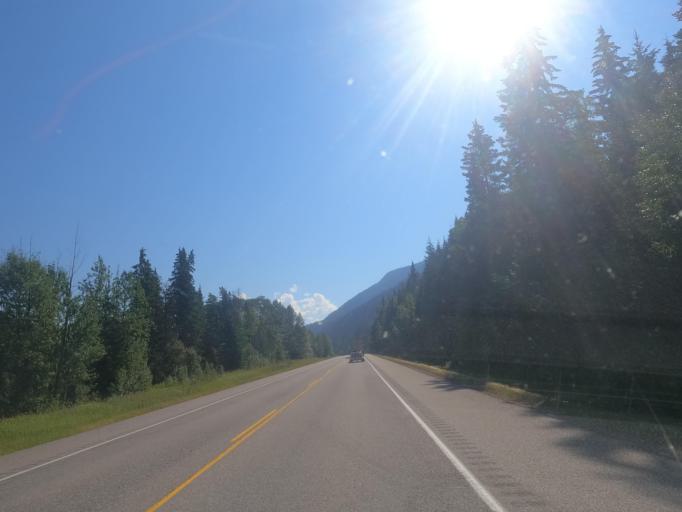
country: CA
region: Alberta
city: Jasper Park Lodge
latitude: 52.8592
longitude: -118.1722
